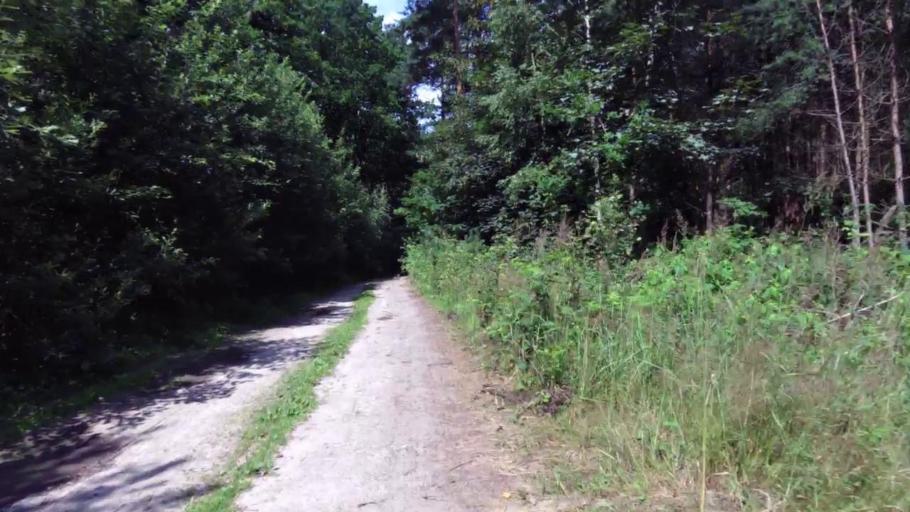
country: PL
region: West Pomeranian Voivodeship
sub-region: Powiat gryfinski
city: Stare Czarnowo
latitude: 53.3474
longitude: 14.7636
